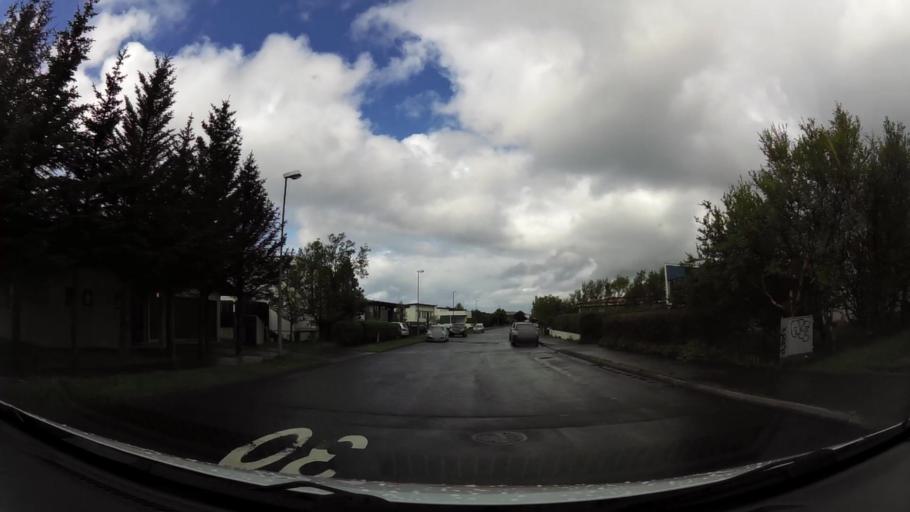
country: IS
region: Capital Region
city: Kopavogur
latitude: 64.1280
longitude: -21.9539
